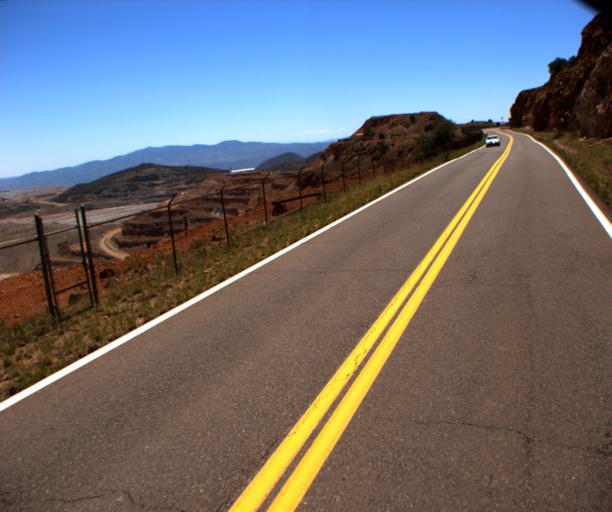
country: US
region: Arizona
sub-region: Greenlee County
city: Morenci
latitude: 33.0928
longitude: -109.3802
